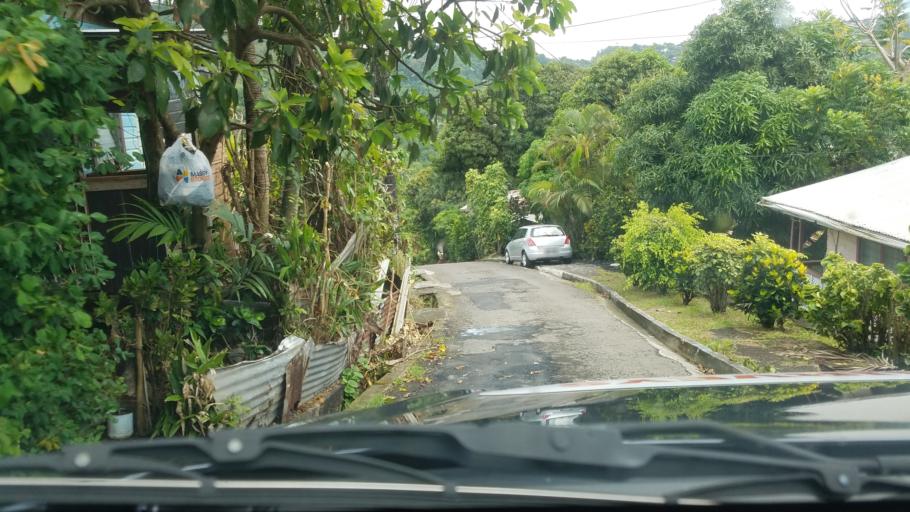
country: LC
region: Castries Quarter
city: Bisee
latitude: 14.0056
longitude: -60.9716
